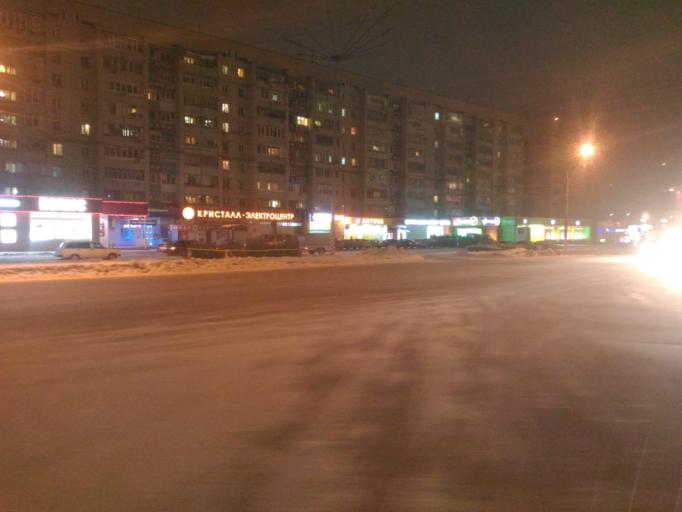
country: RU
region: Ulyanovsk
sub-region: Ulyanovskiy Rayon
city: Ulyanovsk
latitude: 54.3069
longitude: 48.3500
